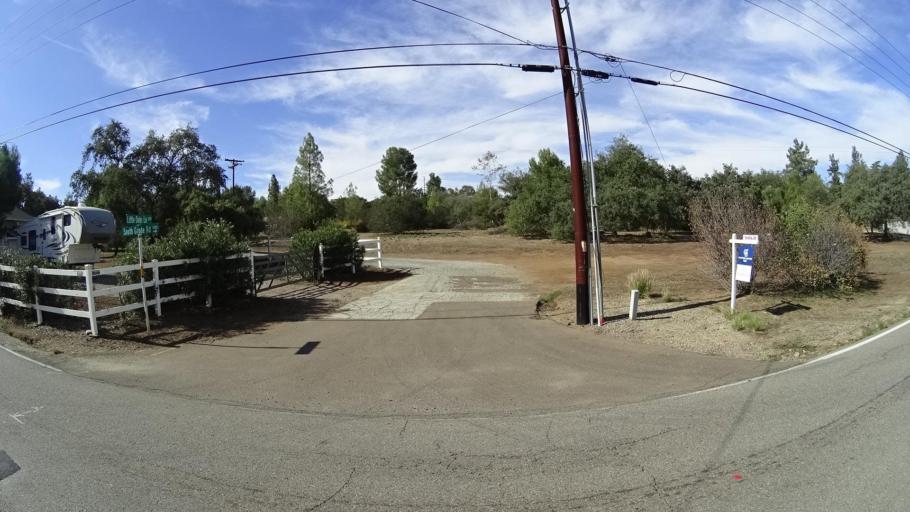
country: US
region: California
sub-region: San Diego County
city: Alpine
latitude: 32.8223
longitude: -116.7869
